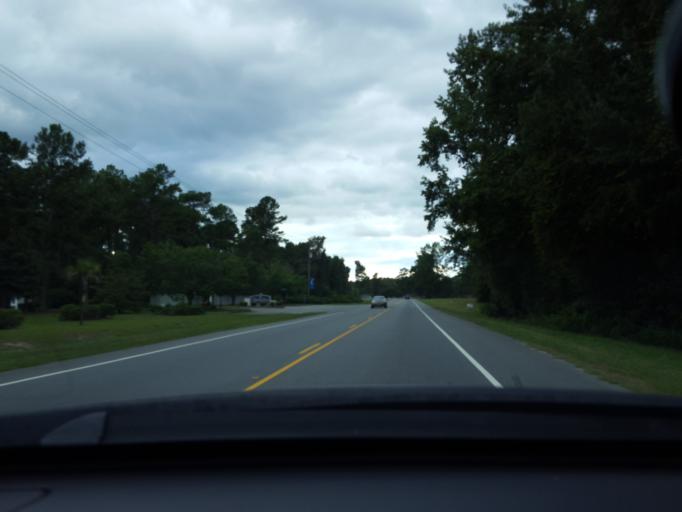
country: US
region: North Carolina
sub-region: Bladen County
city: Elizabethtown
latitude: 34.6556
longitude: -78.5128
